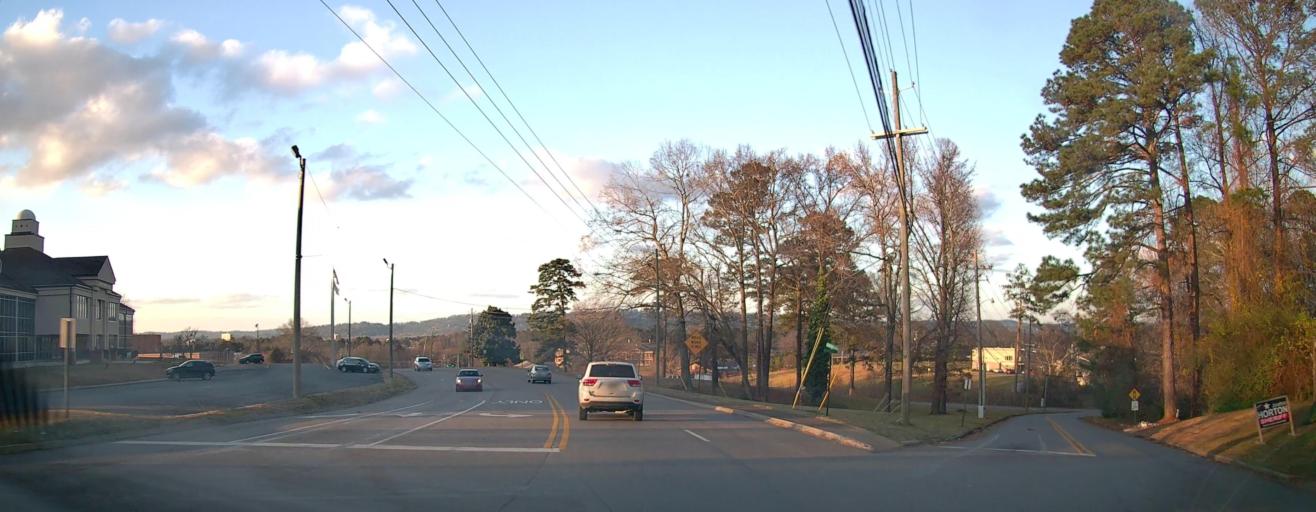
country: US
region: Alabama
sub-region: Etowah County
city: Gadsden
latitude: 33.9941
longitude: -85.9891
